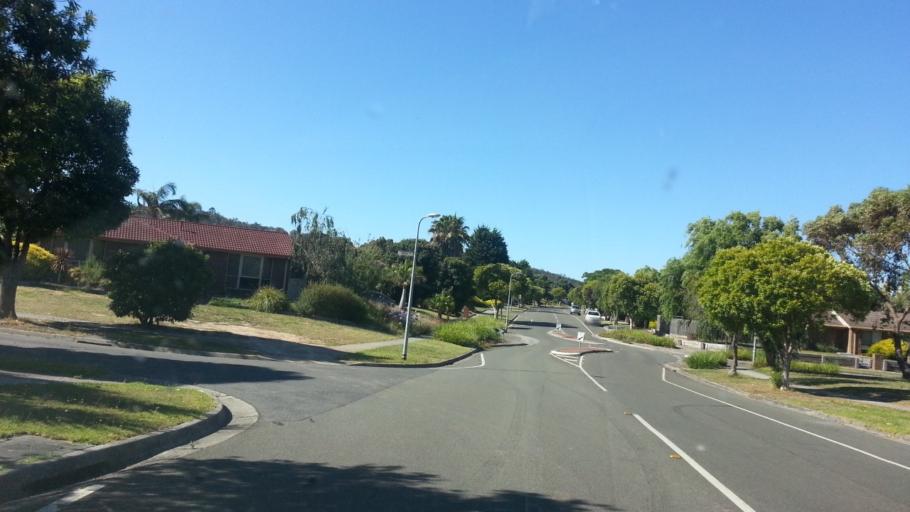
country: AU
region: Victoria
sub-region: Yarra Ranges
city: Lysterfield
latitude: -37.9204
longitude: 145.2690
